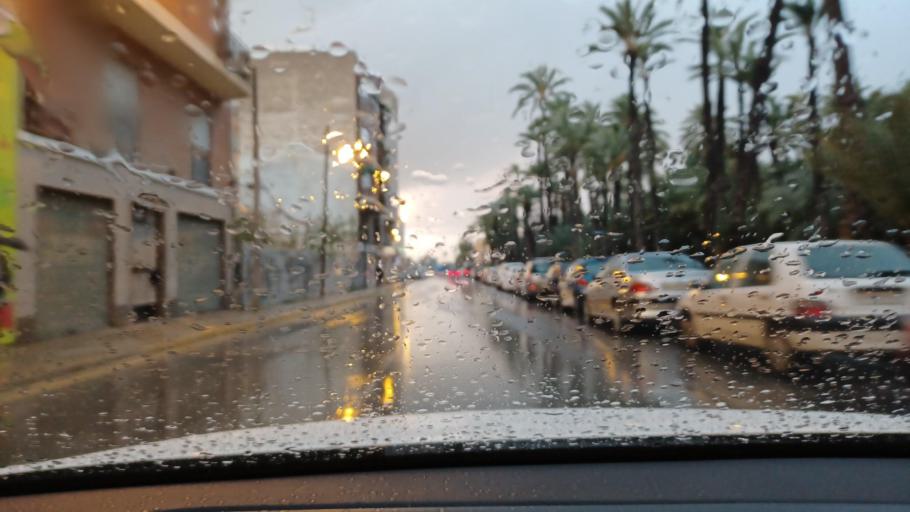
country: ES
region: Valencia
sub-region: Provincia de Alicante
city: Elche
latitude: 38.2559
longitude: -0.6973
